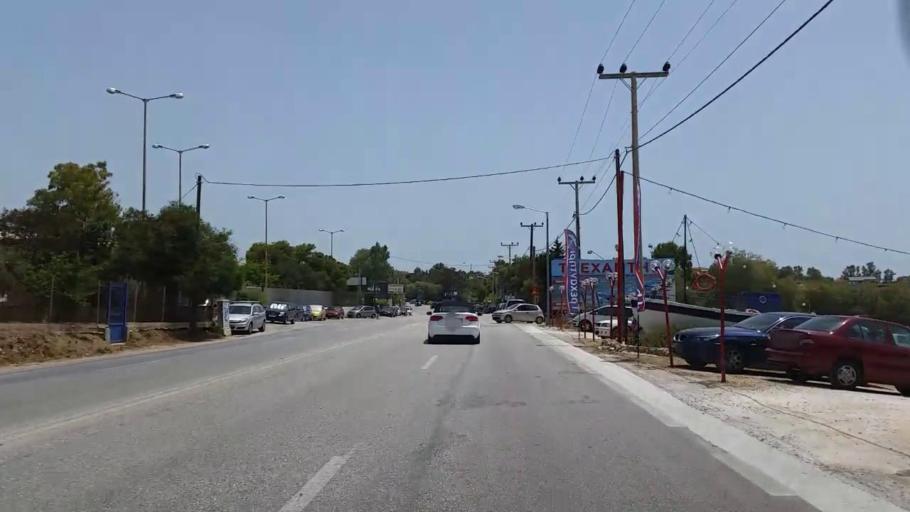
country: GR
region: Attica
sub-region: Nomarchia Anatolikis Attikis
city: Agios Dimitrios Kropias
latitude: 37.7982
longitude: 23.8710
